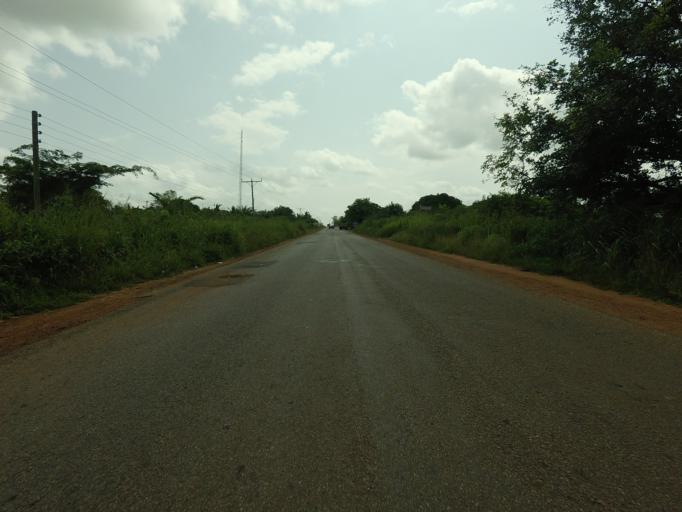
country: TG
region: Maritime
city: Lome
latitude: 6.2249
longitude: 1.0263
